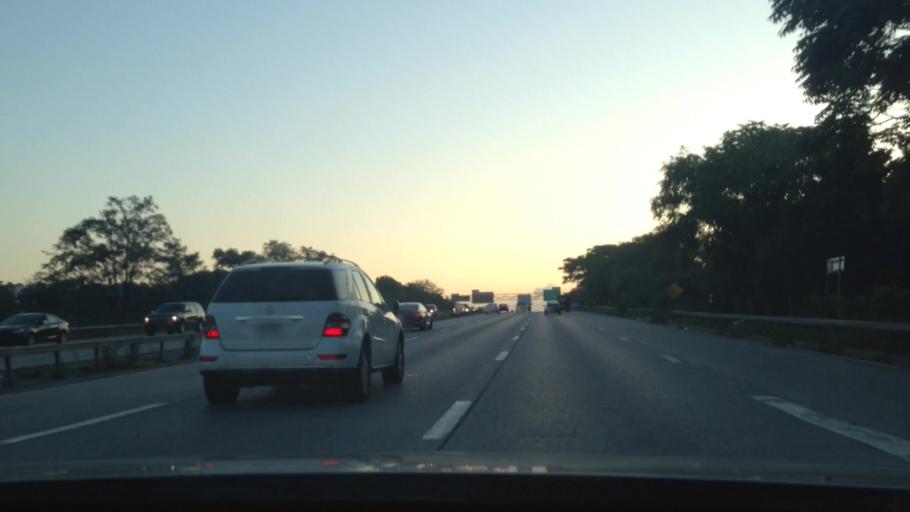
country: US
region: New York
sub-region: Suffolk County
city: Brightwaters
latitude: 40.7303
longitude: -73.2740
